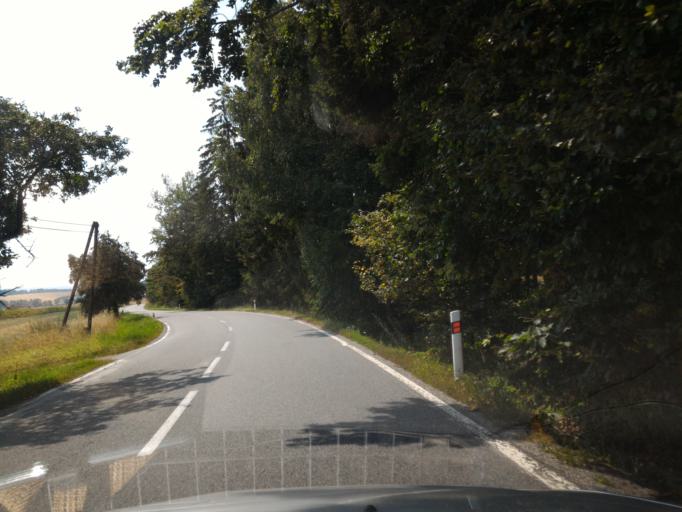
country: CZ
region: Vysocina
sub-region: Okres Jihlava
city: Polna
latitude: 49.4508
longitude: 15.7836
